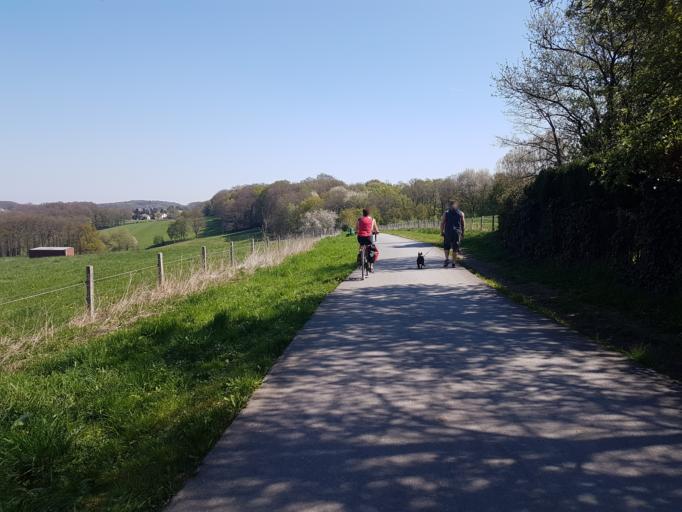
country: DE
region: North Rhine-Westphalia
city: Gevelsberg
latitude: 51.3497
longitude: 7.3093
